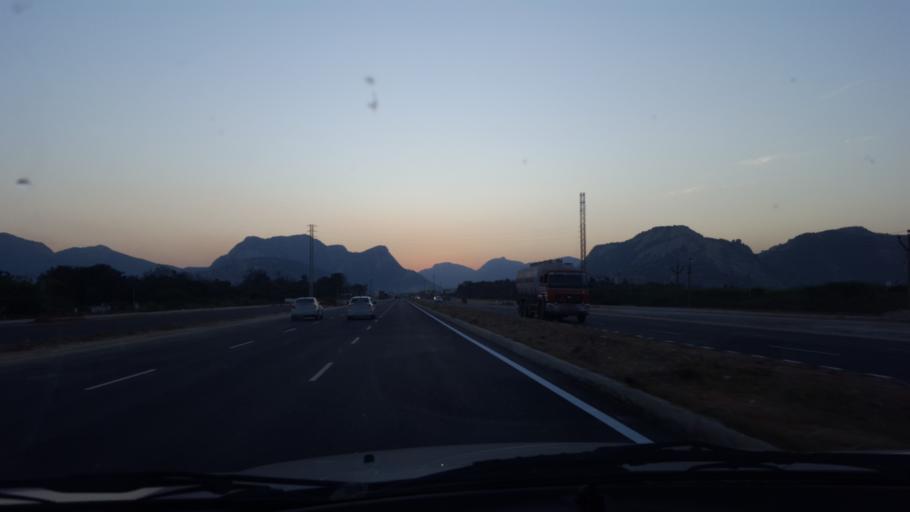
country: IN
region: Andhra Pradesh
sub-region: Chittoor
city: Narasingapuram
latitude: 13.5845
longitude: 79.3283
